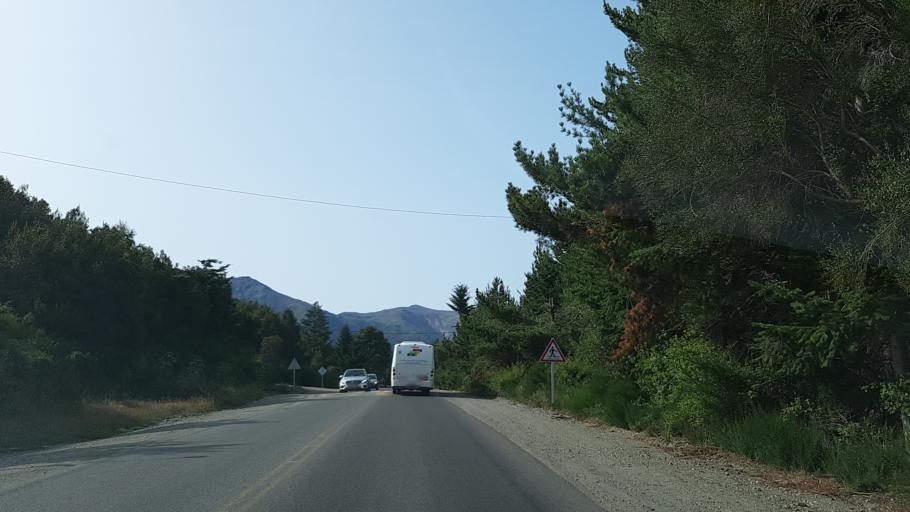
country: AR
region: Rio Negro
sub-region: Departamento de Bariloche
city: San Carlos de Bariloche
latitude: -41.1481
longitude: -71.4095
